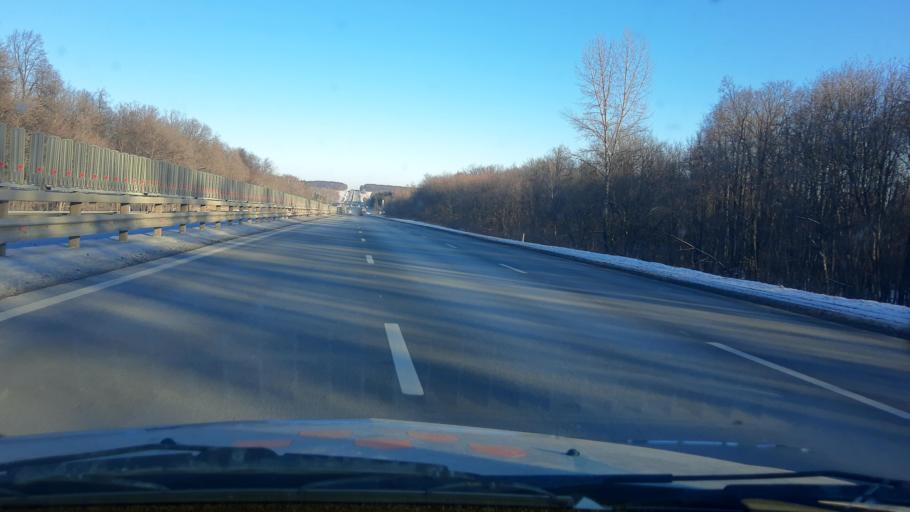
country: RU
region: Bashkortostan
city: Avdon
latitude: 54.6456
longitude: 55.6340
